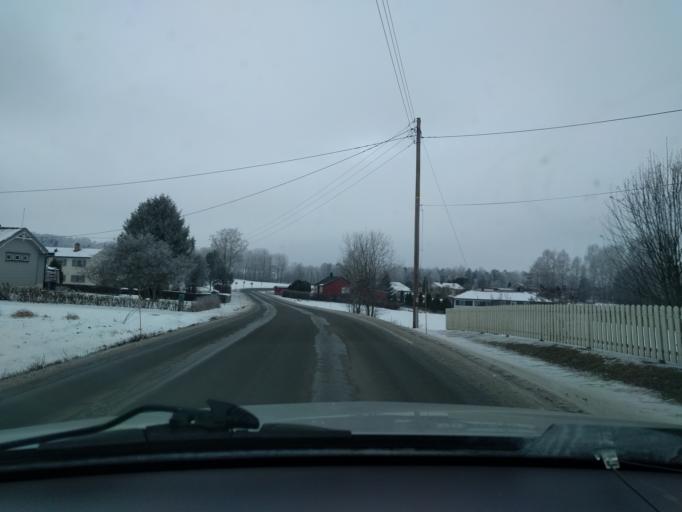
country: NO
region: Hedmark
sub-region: Hamar
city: Hamar
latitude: 60.7856
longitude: 11.1481
